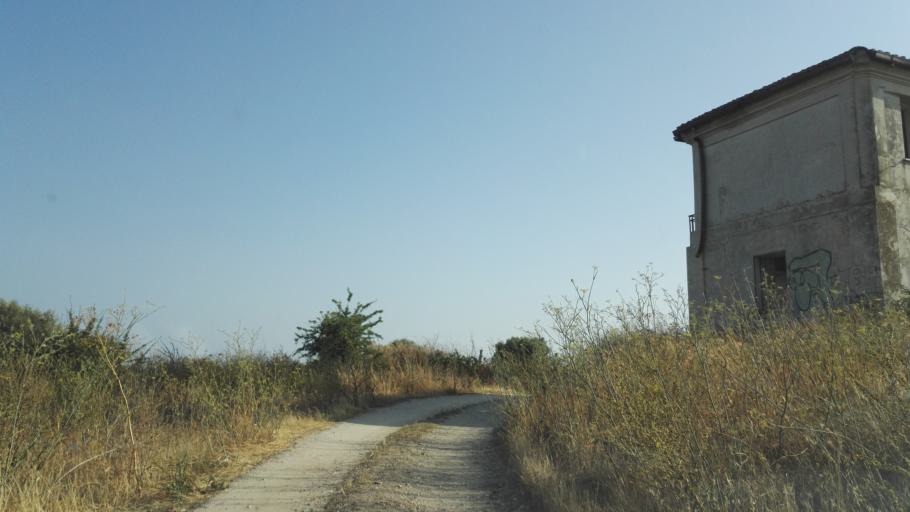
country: IT
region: Calabria
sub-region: Provincia di Reggio Calabria
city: Riace Marina
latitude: 38.3719
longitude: 16.4955
